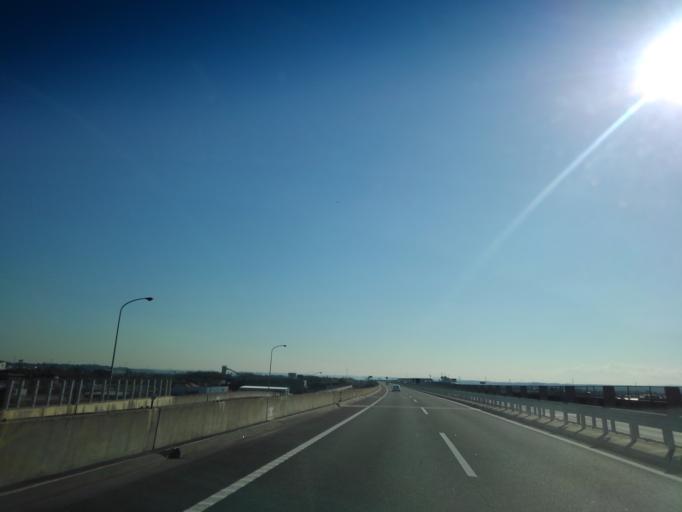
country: JP
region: Chiba
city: Kisarazu
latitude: 35.4211
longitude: 139.9379
